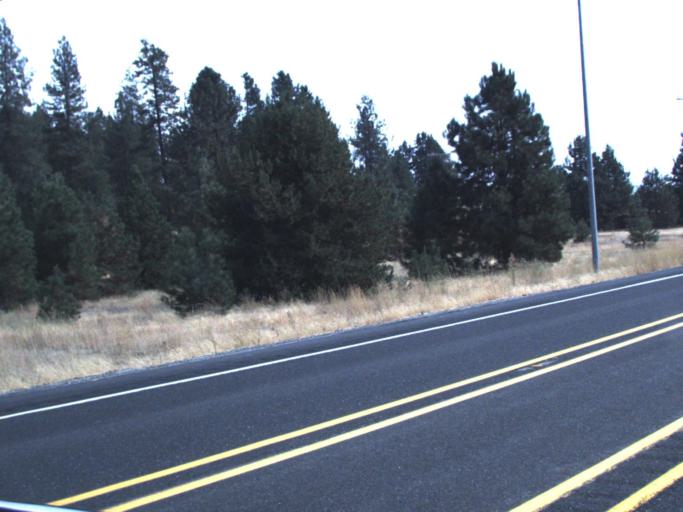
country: US
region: Washington
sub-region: Spokane County
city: Deer Park
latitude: 47.9186
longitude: -117.4542
